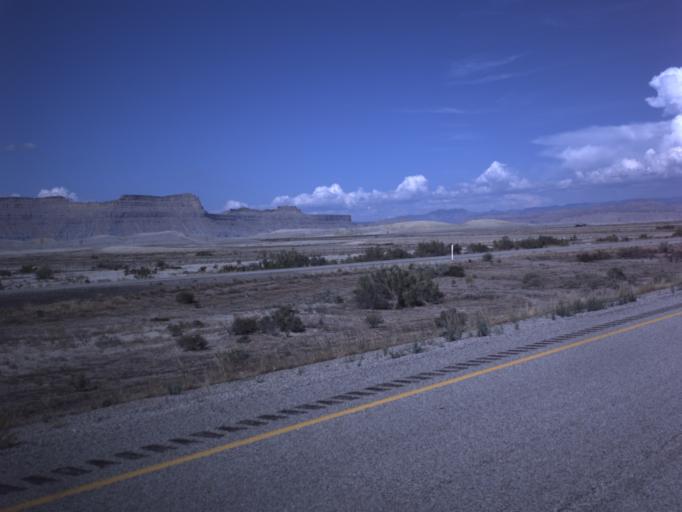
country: US
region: Utah
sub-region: Carbon County
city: East Carbon City
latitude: 38.9781
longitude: -110.2420
